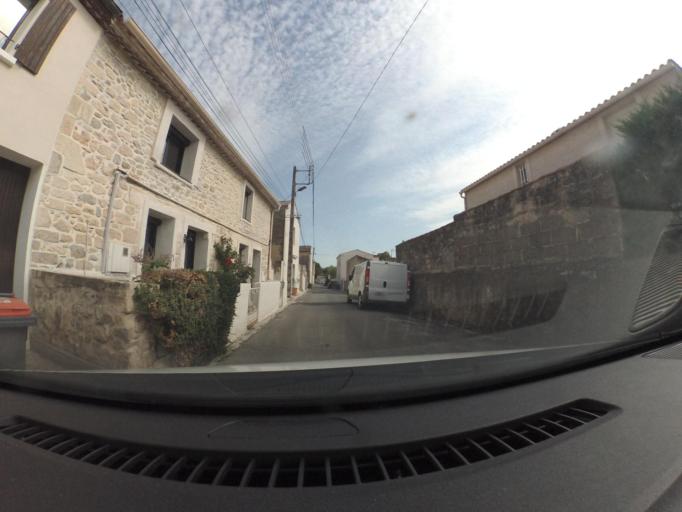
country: FR
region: Languedoc-Roussillon
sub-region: Departement de l'Herault
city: Baillargues
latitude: 43.6628
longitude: 4.0118
